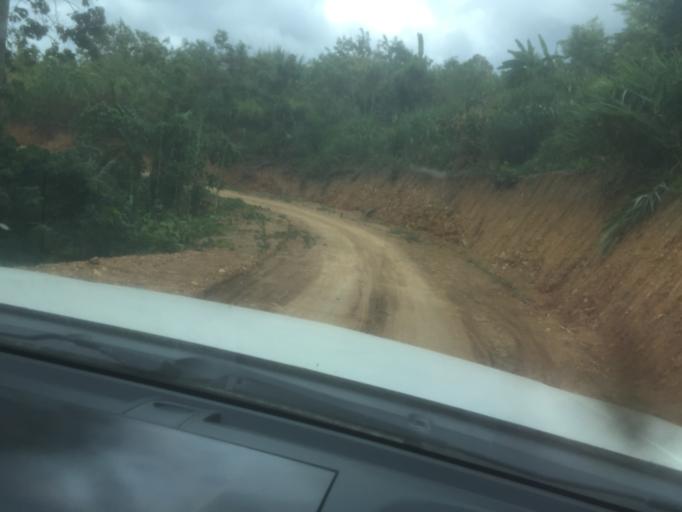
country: LA
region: Phongsali
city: Khoa
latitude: 20.9259
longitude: 102.5430
